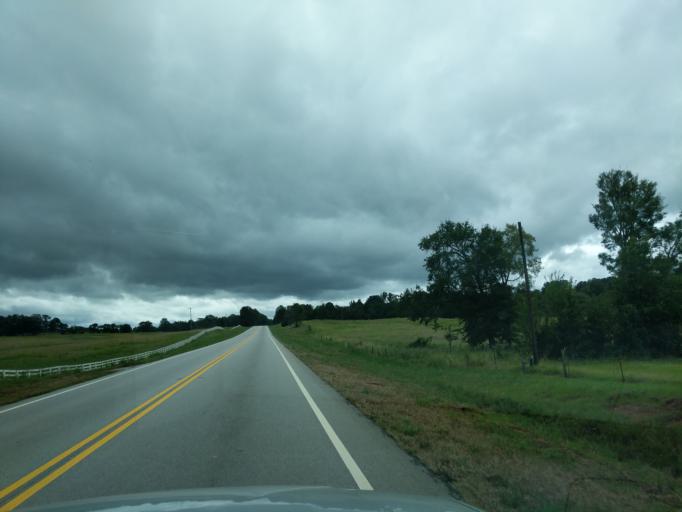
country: US
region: Georgia
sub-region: Wilkes County
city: Washington
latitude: 33.9218
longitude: -82.7532
